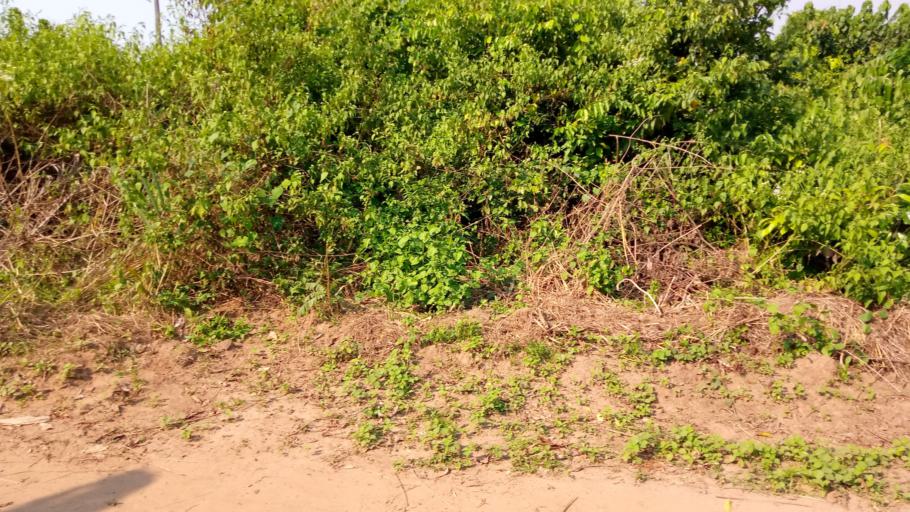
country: CD
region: Bandundu
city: Bulungu
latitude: -4.6304
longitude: 18.6718
